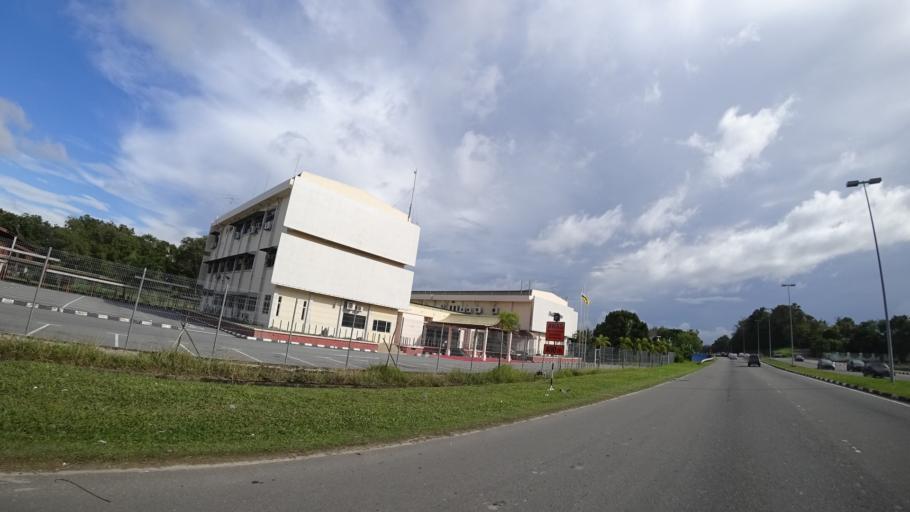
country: BN
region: Brunei and Muara
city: Bandar Seri Begawan
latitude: 4.8924
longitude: 114.8985
